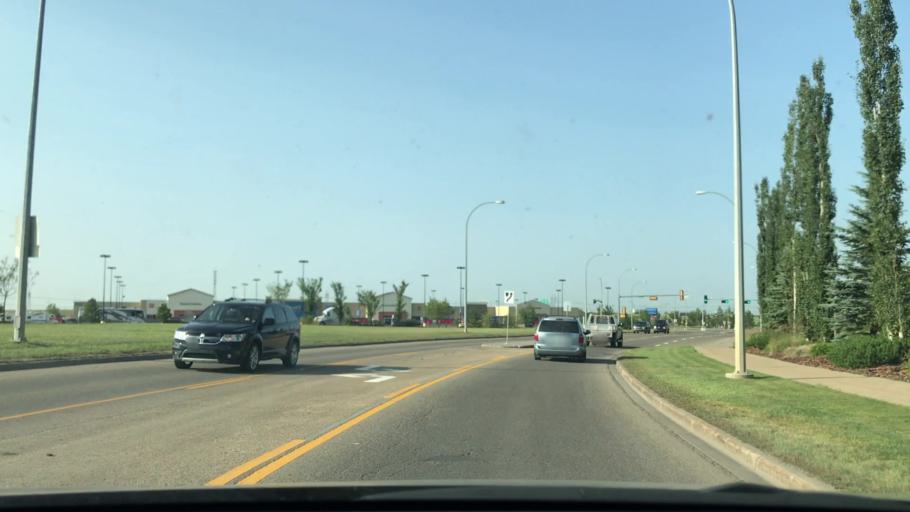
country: CA
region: Alberta
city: Edmonton
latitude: 53.4437
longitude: -113.4809
